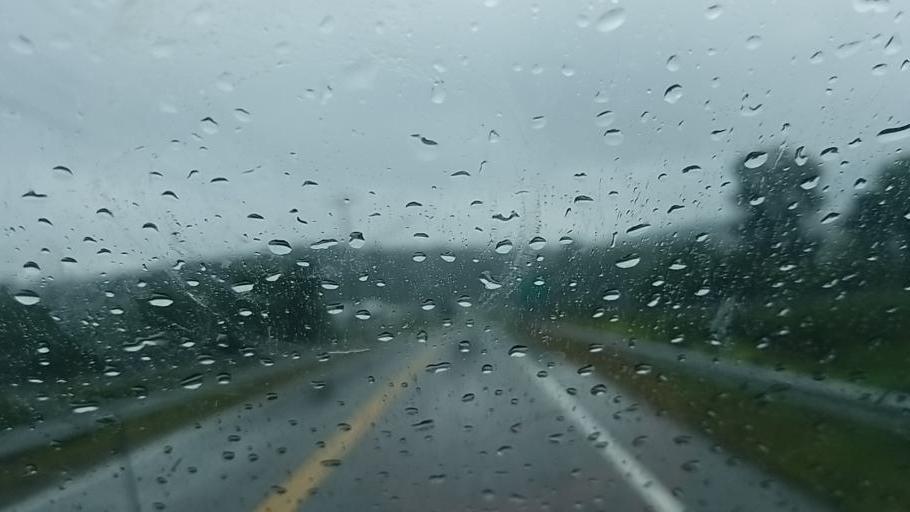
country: US
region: Ohio
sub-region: Logan County
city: Bellefontaine
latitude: 40.3254
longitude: -83.6631
